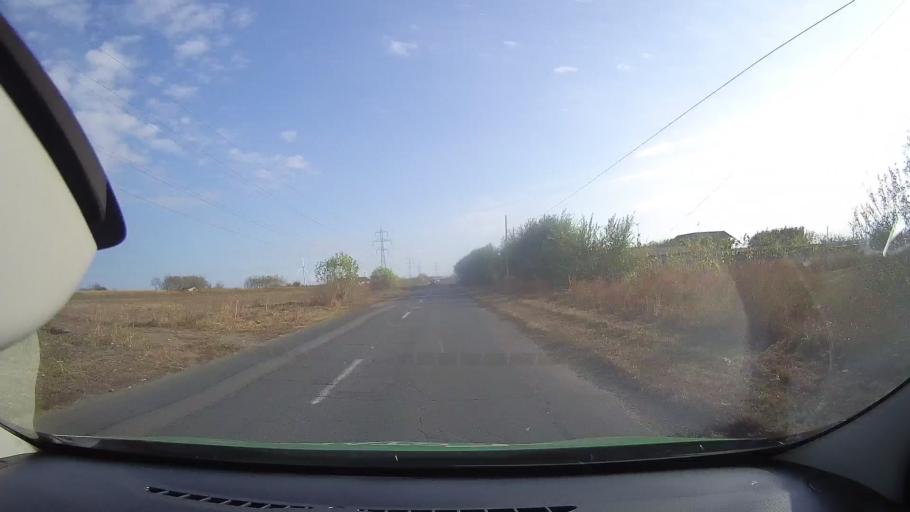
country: RO
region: Constanta
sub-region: Comuna Corbu
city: Corbu
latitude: 44.3712
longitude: 28.6671
